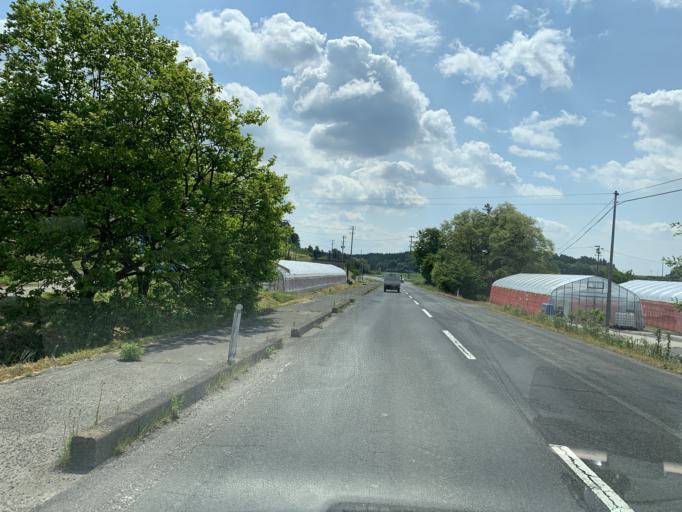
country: JP
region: Miyagi
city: Furukawa
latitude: 38.6848
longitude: 140.9555
